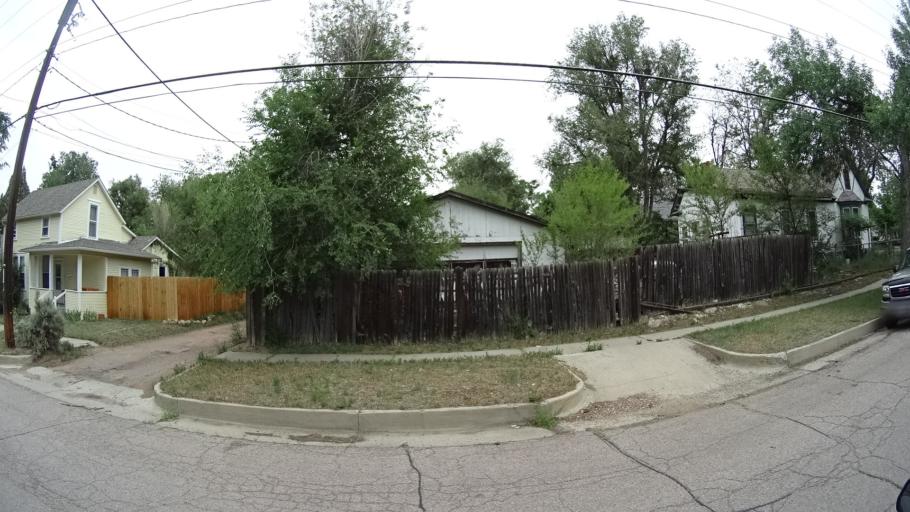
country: US
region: Colorado
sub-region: El Paso County
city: Colorado Springs
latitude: 38.8439
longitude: -104.8103
